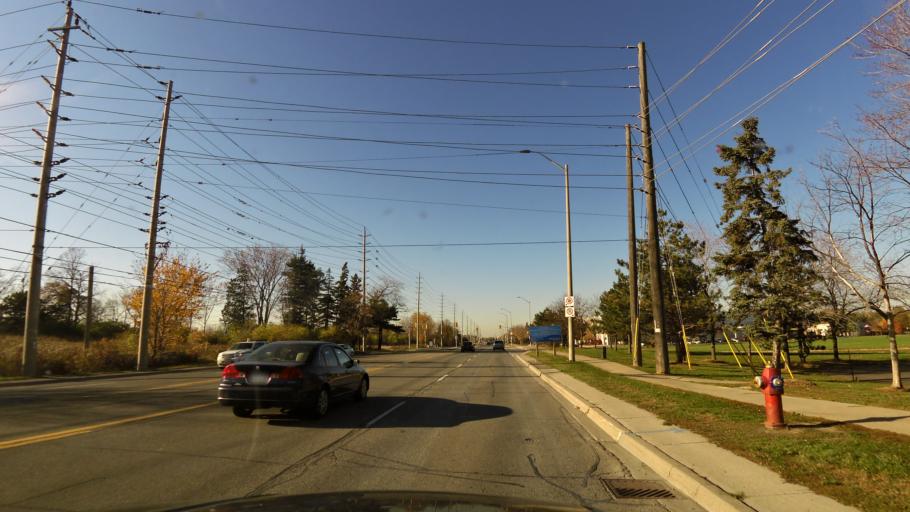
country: CA
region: Ontario
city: Mississauga
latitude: 43.6231
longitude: -79.6247
